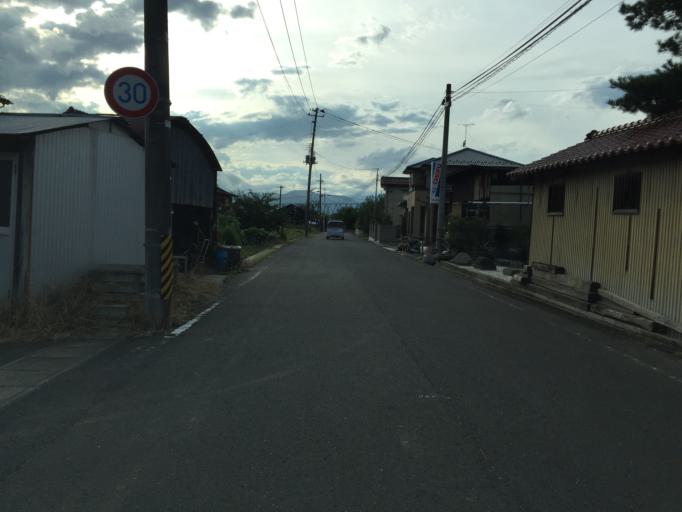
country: JP
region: Fukushima
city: Hobaramachi
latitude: 37.8048
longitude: 140.5110
